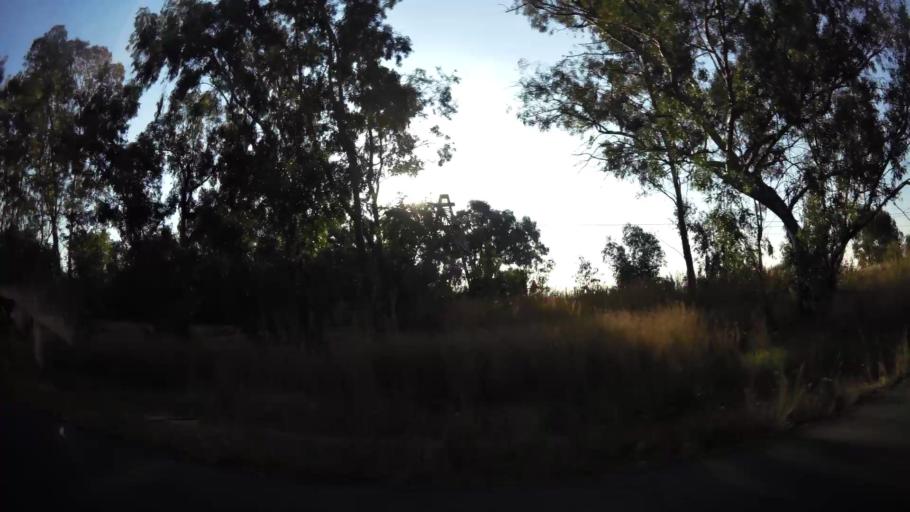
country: ZA
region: Gauteng
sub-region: West Rand District Municipality
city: Randfontein
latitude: -26.1955
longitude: 27.6797
